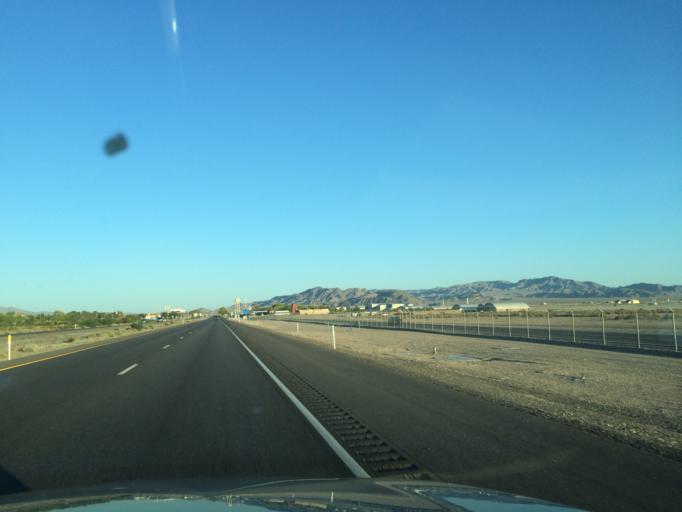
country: US
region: Nevada
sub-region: Nye County
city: Pahrump
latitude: 36.5776
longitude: -115.6608
